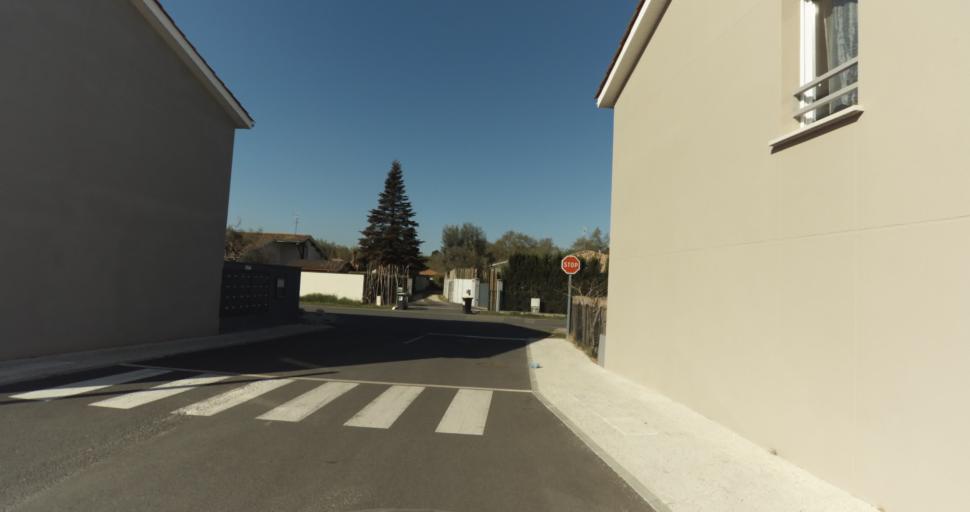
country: FR
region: Aquitaine
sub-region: Departement de la Gironde
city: Martignas-sur-Jalle
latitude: 44.7991
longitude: -0.8373
